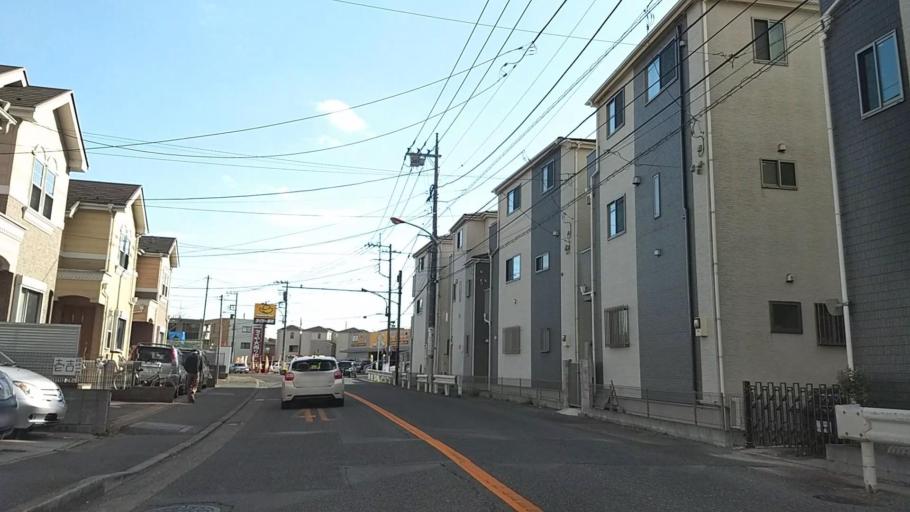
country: JP
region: Tokyo
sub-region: Machida-shi
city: Machida
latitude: 35.5833
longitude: 139.4972
